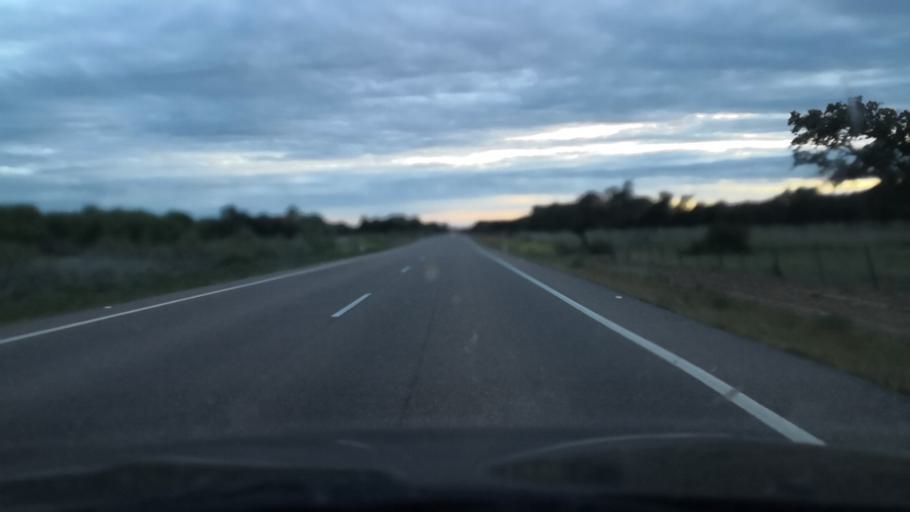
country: ES
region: Extremadura
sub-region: Provincia de Badajoz
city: La Roca de la Sierra
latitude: 39.0879
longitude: -6.7265
